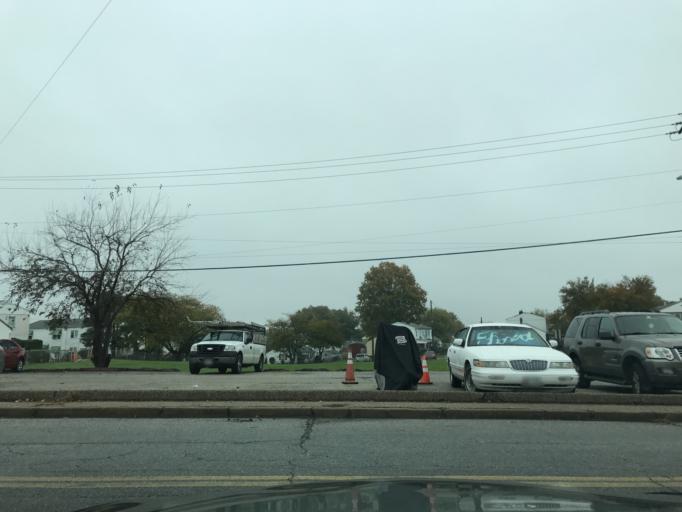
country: US
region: Maryland
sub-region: Baltimore County
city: Rosedale
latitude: 39.3044
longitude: -76.5489
